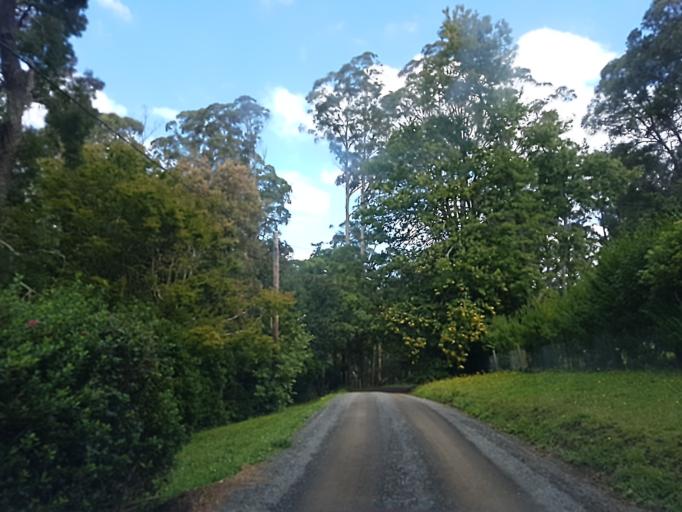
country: AU
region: Victoria
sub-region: Yarra Ranges
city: Kallista
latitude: -37.8852
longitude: 145.3768
